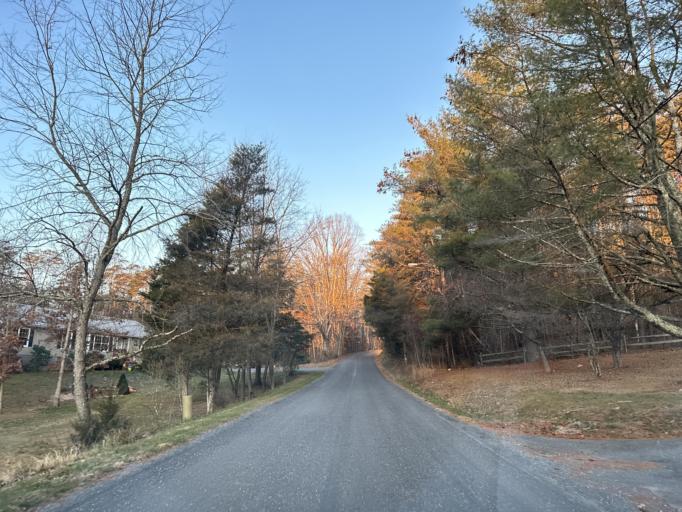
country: US
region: Virginia
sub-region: Rockbridge County
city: East Lexington
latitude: 38.0790
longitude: -79.3876
